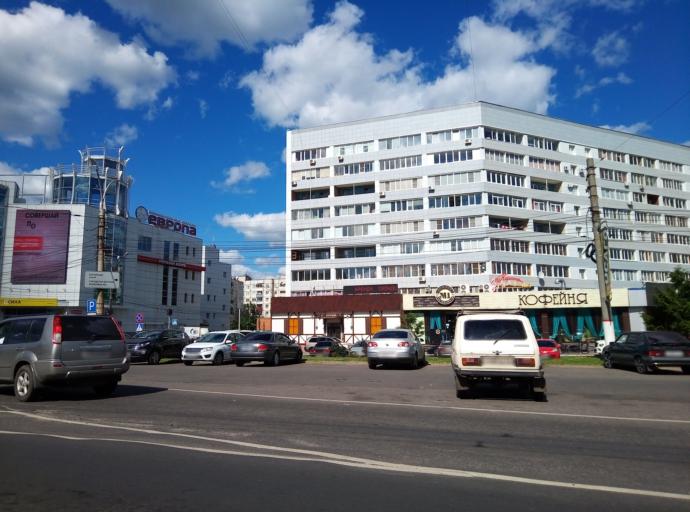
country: RU
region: Kursk
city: Kursk
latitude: 51.7572
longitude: 36.1882
